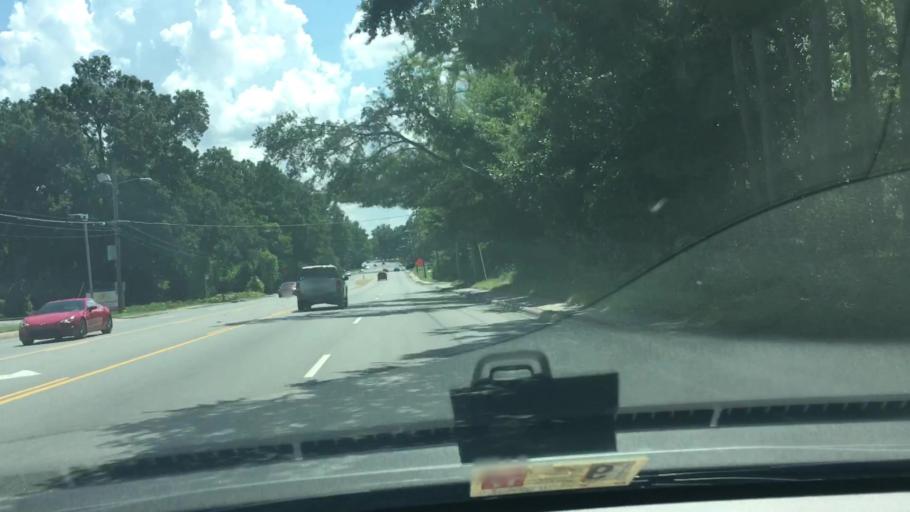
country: US
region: North Carolina
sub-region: Mecklenburg County
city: Charlotte
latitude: 35.2656
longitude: -80.7951
